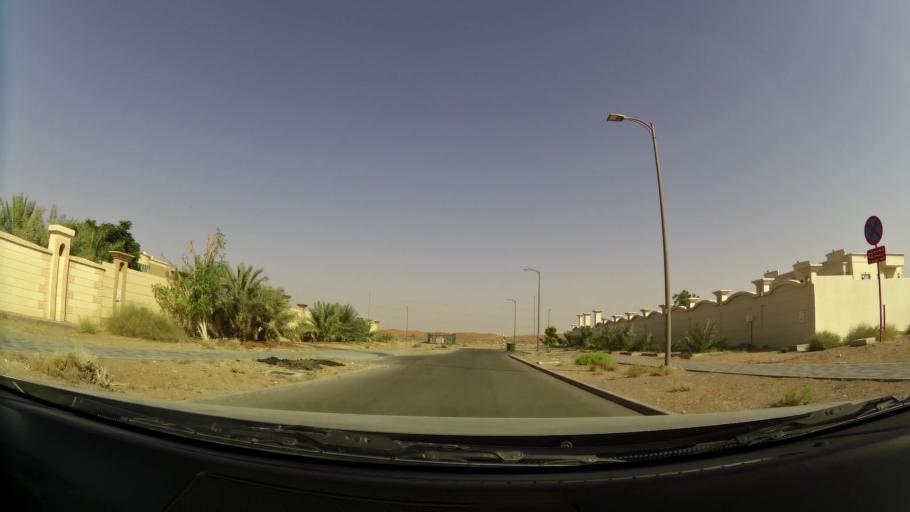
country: OM
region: Al Buraimi
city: Al Buraymi
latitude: 24.3626
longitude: 55.7915
